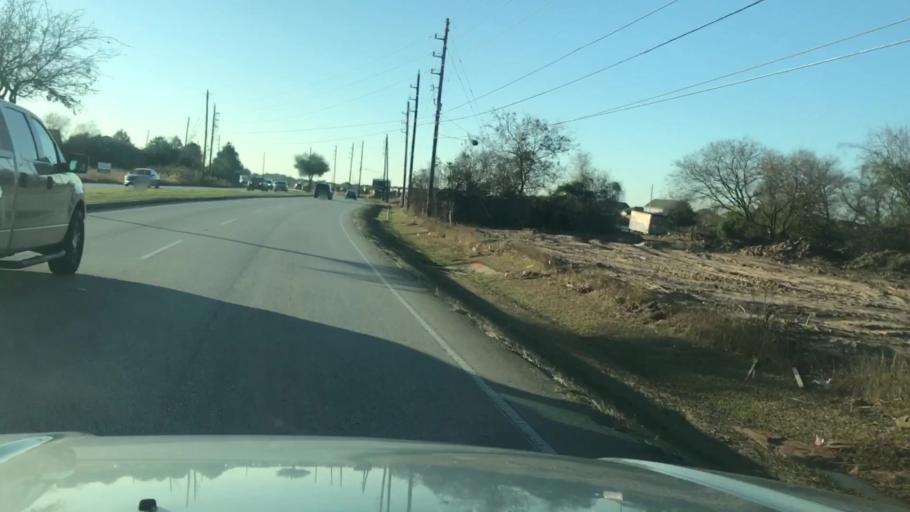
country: US
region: Texas
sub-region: Fort Bend County
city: Cinco Ranch
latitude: 29.8314
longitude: -95.7383
